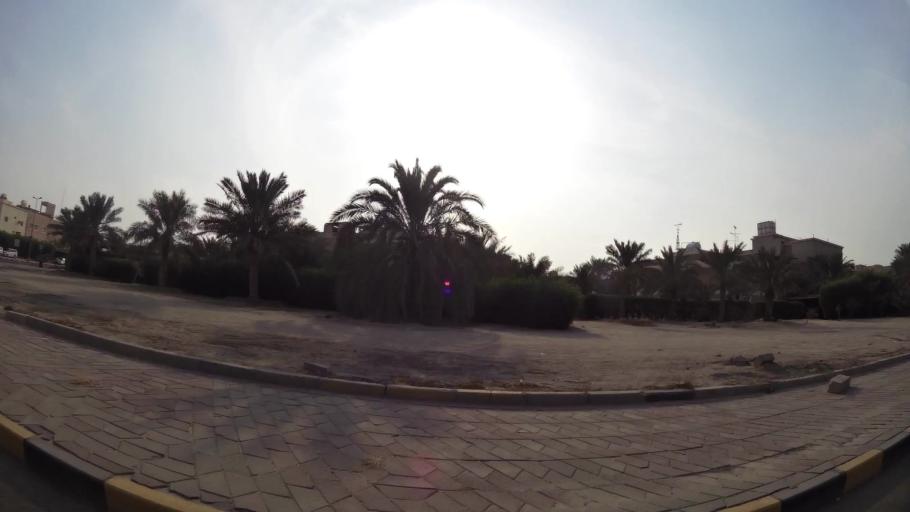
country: KW
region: Mubarak al Kabir
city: Sabah as Salim
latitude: 29.2533
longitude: 48.0558
